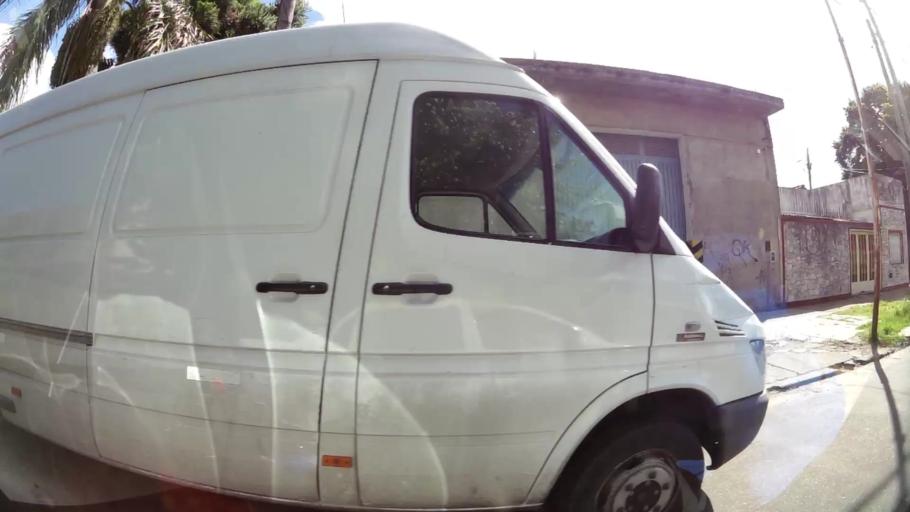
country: AR
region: Buenos Aires
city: San Justo
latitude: -34.6560
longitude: -58.5443
